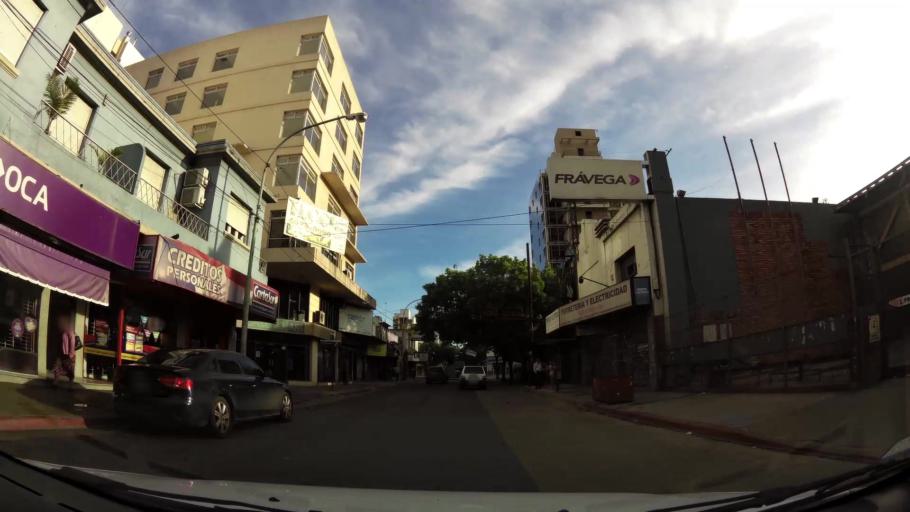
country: AR
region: Buenos Aires
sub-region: Partido de Moron
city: Moron
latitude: -34.6508
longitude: -58.6186
